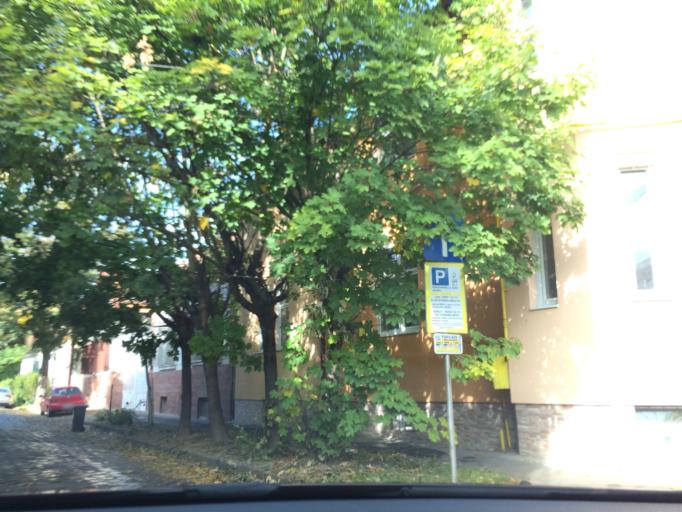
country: RO
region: Timis
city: Timisoara
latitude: 45.7434
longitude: 21.2336
